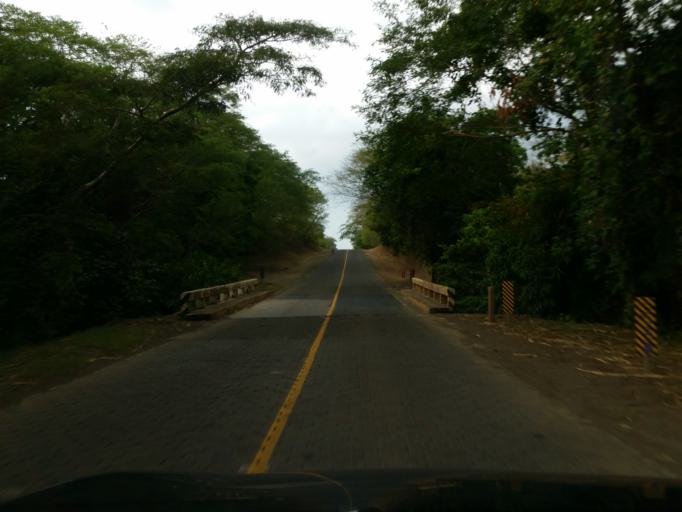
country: NI
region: Managua
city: Carlos Fonseca Amador
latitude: 12.0056
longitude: -86.5172
